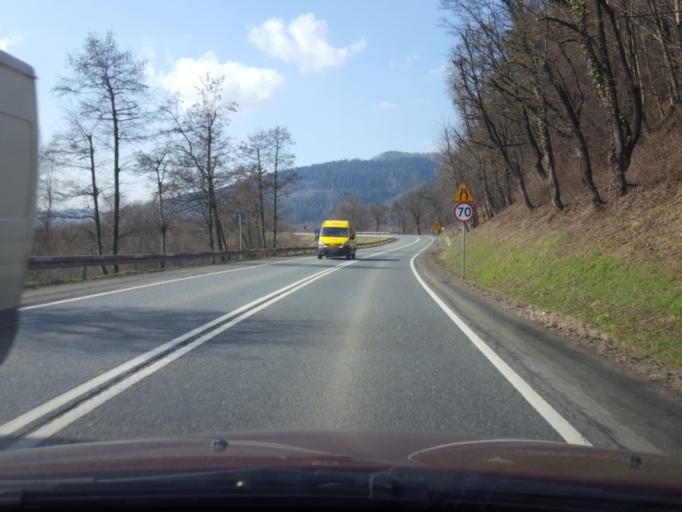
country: PL
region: Lesser Poland Voivodeship
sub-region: Powiat nowosadecki
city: Lososina Dolna
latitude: 49.6933
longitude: 20.6569
